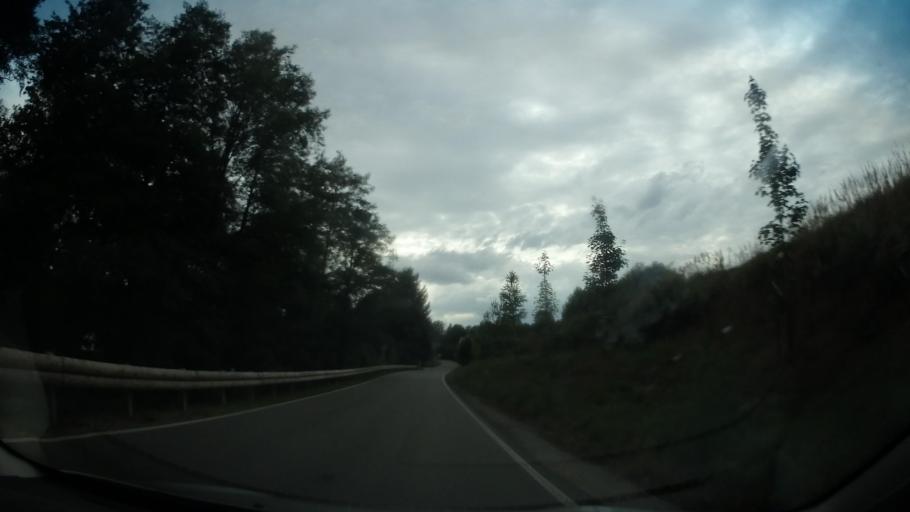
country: CZ
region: Pardubicky
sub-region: Okres Chrudim
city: Nasavrky
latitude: 49.8026
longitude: 15.7693
